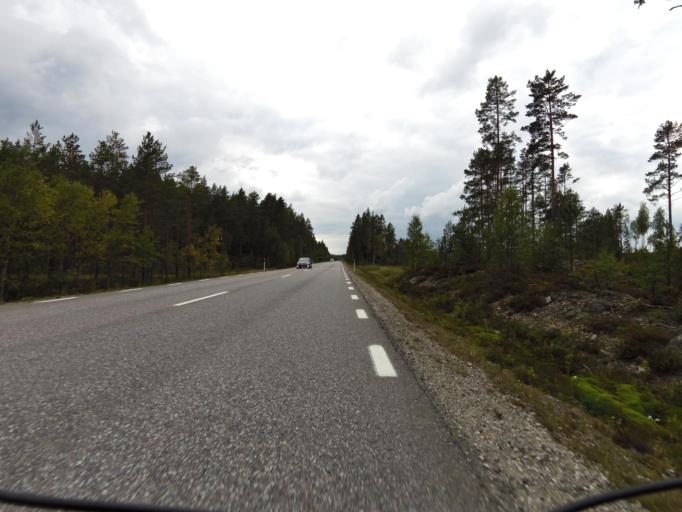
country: SE
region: Gaevleborg
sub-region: Ockelbo Kommun
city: Ockelbo
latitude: 60.8786
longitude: 16.8610
